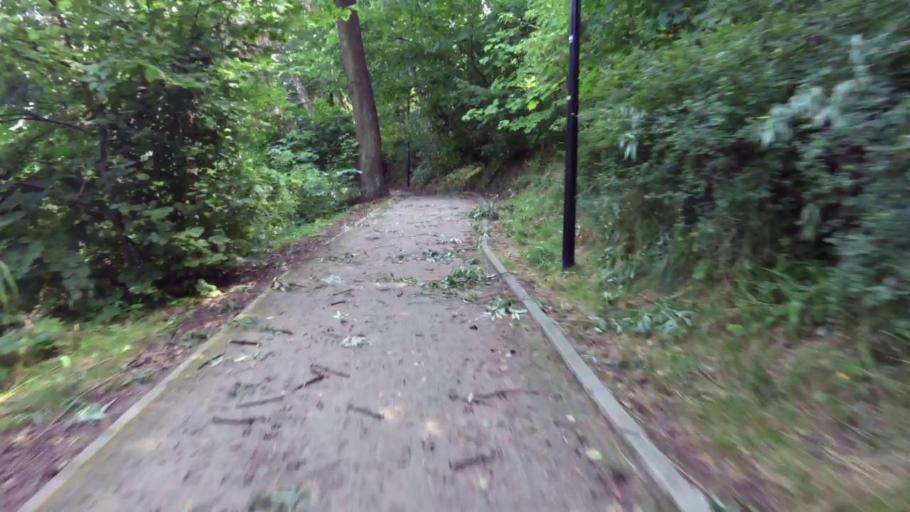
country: PL
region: West Pomeranian Voivodeship
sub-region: Powiat choszczenski
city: Choszczno
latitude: 53.1579
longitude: 15.4234
